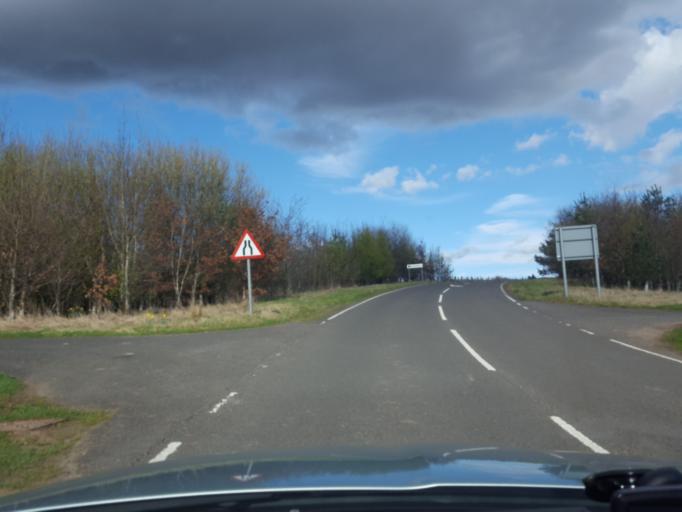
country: GB
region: Scotland
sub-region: Perth and Kinross
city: Abernethy
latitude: 56.3832
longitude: -3.3489
